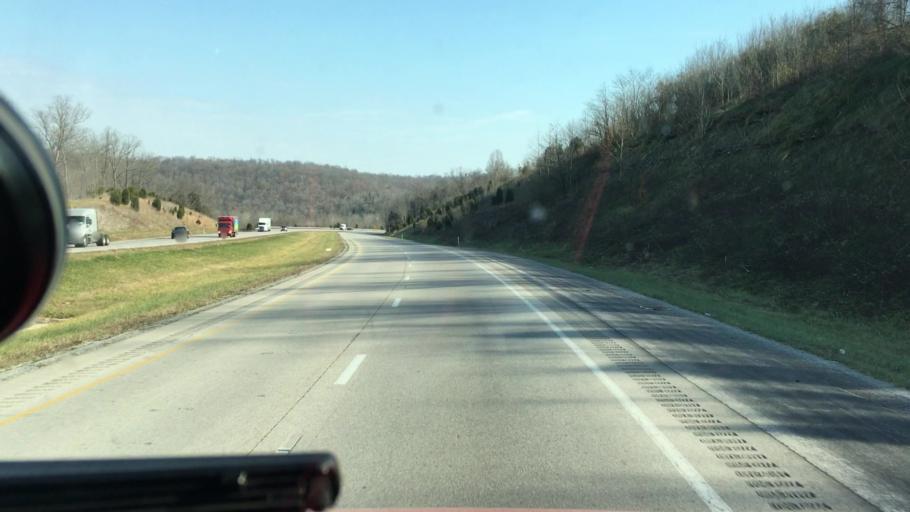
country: US
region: Kentucky
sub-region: Bath County
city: Owingsville
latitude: 38.1237
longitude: -83.7814
